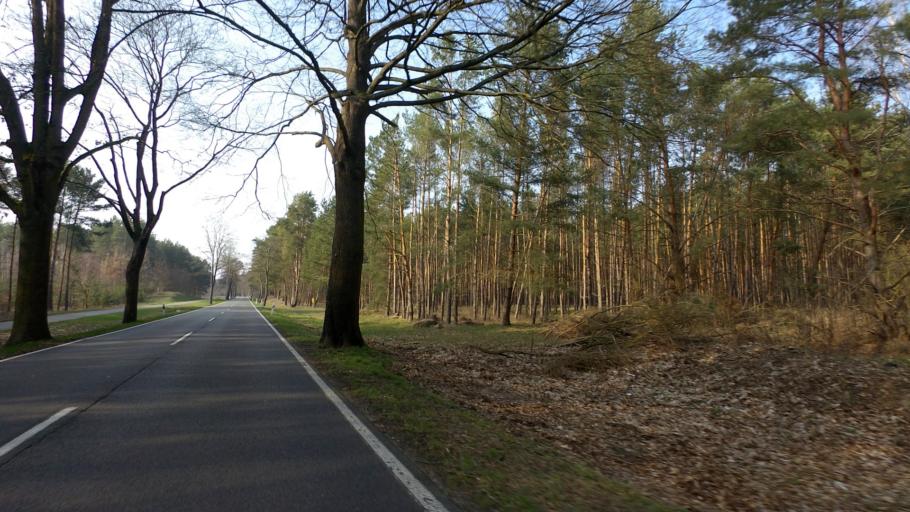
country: DE
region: Brandenburg
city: Beelitz
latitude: 52.1722
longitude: 13.0546
